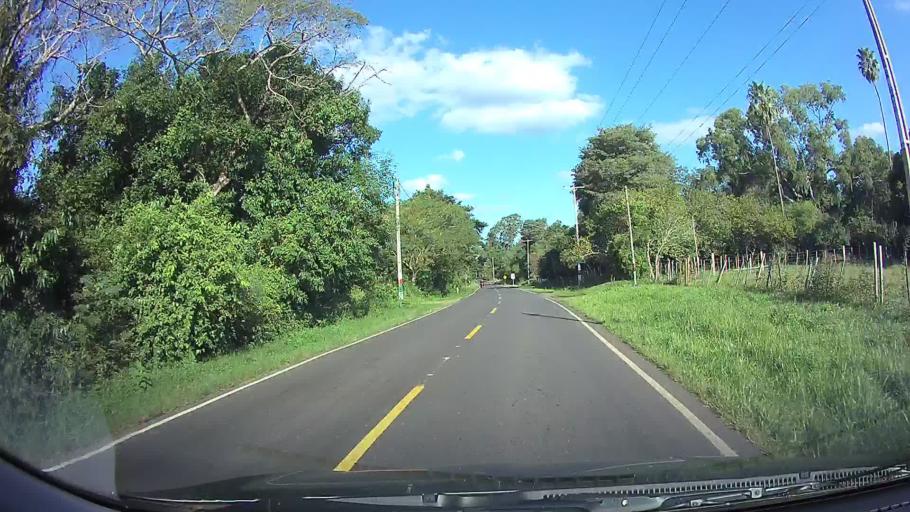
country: PY
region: Central
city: Aregua
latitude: -25.2914
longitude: -57.3940
